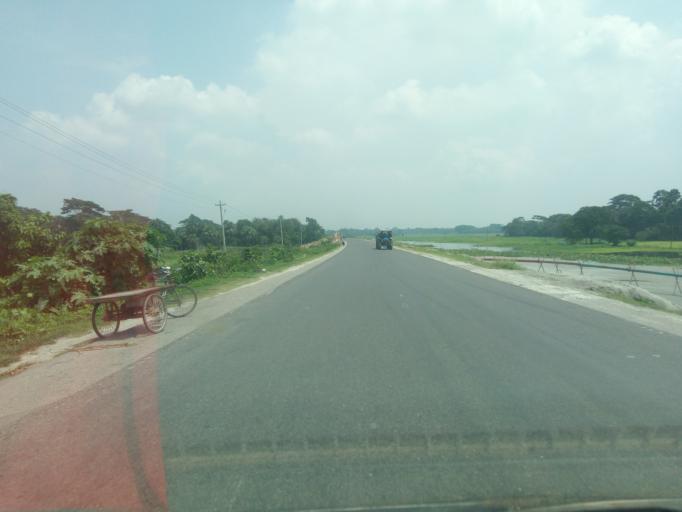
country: BD
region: Dhaka
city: Char Bhadrasan
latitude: 23.3805
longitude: 90.0062
